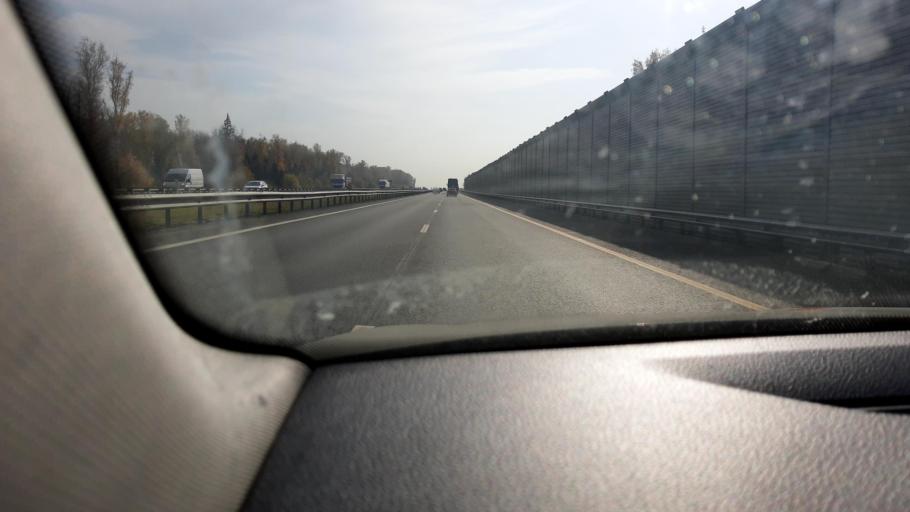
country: RU
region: Moskovskaya
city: Mikhnevo
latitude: 55.0611
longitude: 37.9330
